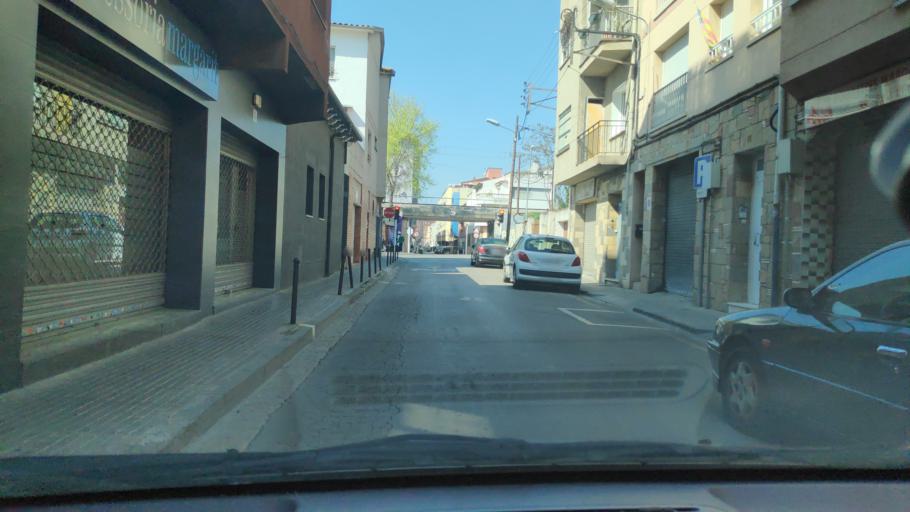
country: ES
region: Catalonia
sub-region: Provincia de Barcelona
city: Mollet del Valles
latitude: 41.5421
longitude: 2.2105
